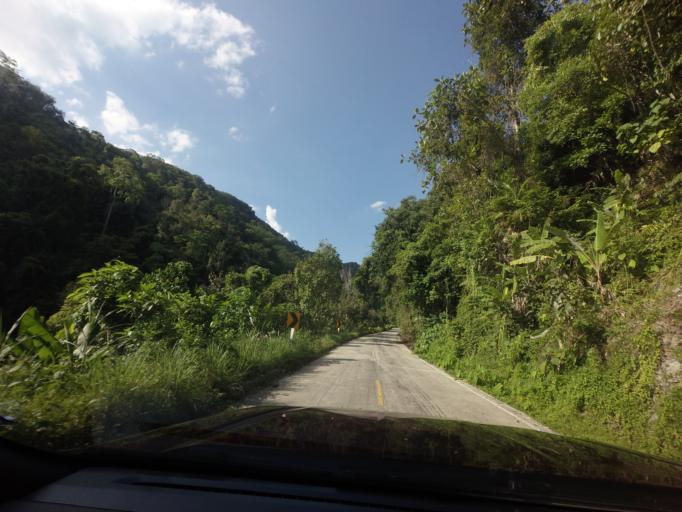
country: TH
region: Yala
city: Than To
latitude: 6.1336
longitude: 101.2991
